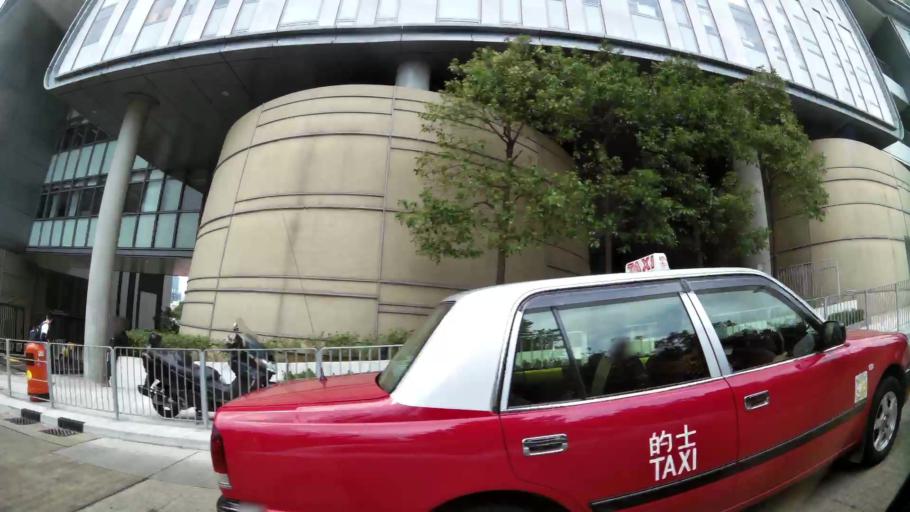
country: HK
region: Sham Shui Po
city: Sham Shui Po
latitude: 22.3383
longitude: 114.1724
